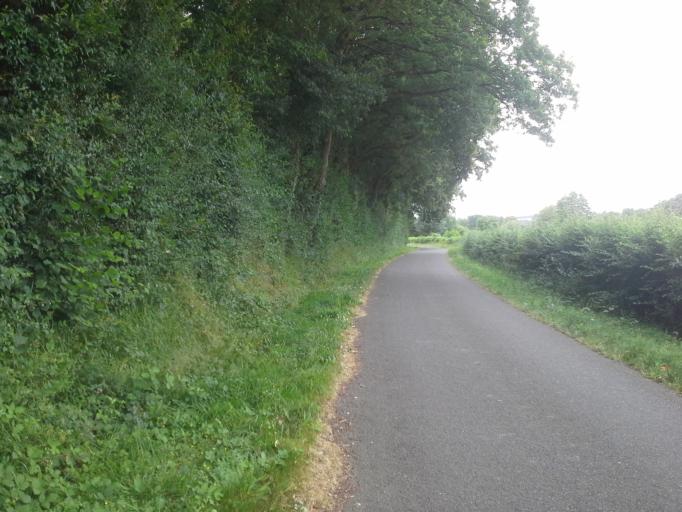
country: FR
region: Centre
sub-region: Departement du Loir-et-Cher
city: Mondoubleau
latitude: 48.0025
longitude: 0.8224
